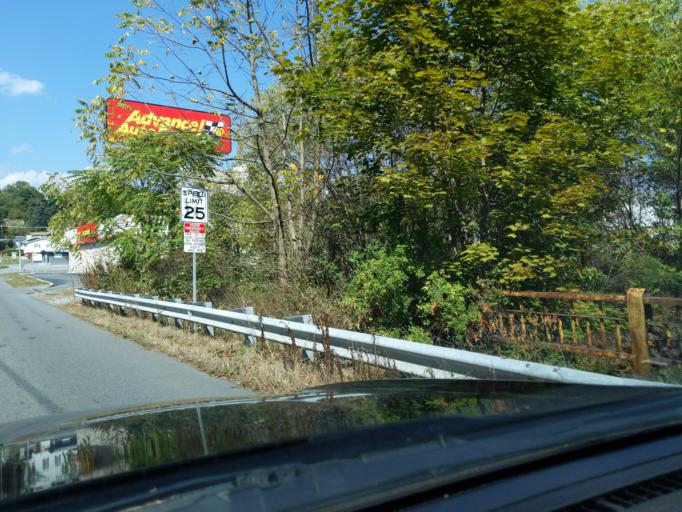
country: US
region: Pennsylvania
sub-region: Blair County
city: Altoona
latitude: 40.5100
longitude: -78.3806
